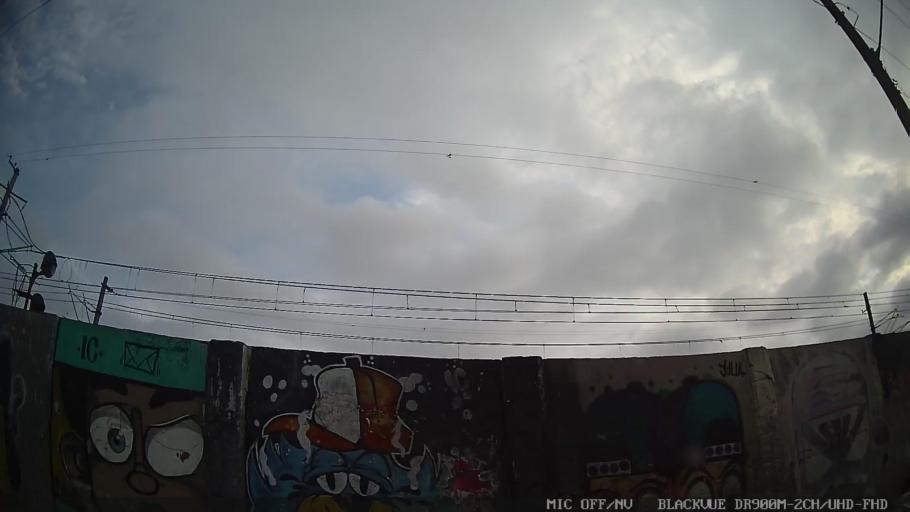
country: BR
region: Sao Paulo
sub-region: Itaquaquecetuba
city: Itaquaquecetuba
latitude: -23.4936
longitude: -46.4100
